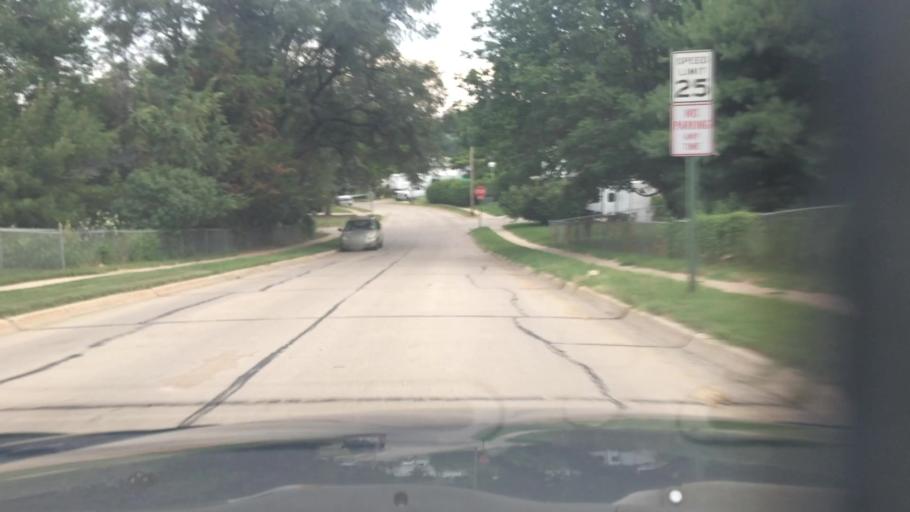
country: US
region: Nebraska
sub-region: Douglas County
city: Ralston
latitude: 41.1875
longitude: -96.0512
